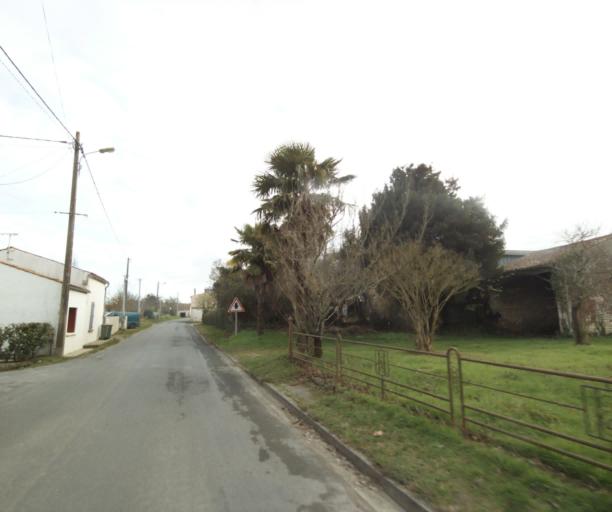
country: FR
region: Poitou-Charentes
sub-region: Departement de la Charente-Maritime
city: Corme-Royal
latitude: 45.7231
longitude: -0.8267
